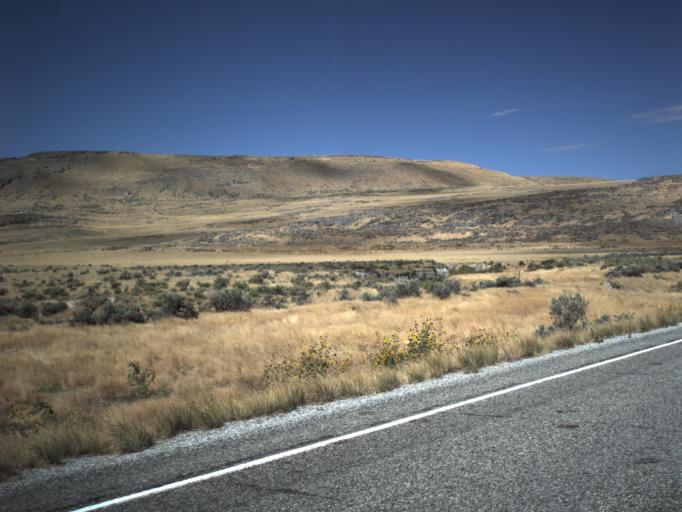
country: US
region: Utah
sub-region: Box Elder County
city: Tremonton
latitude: 41.6660
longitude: -112.4450
